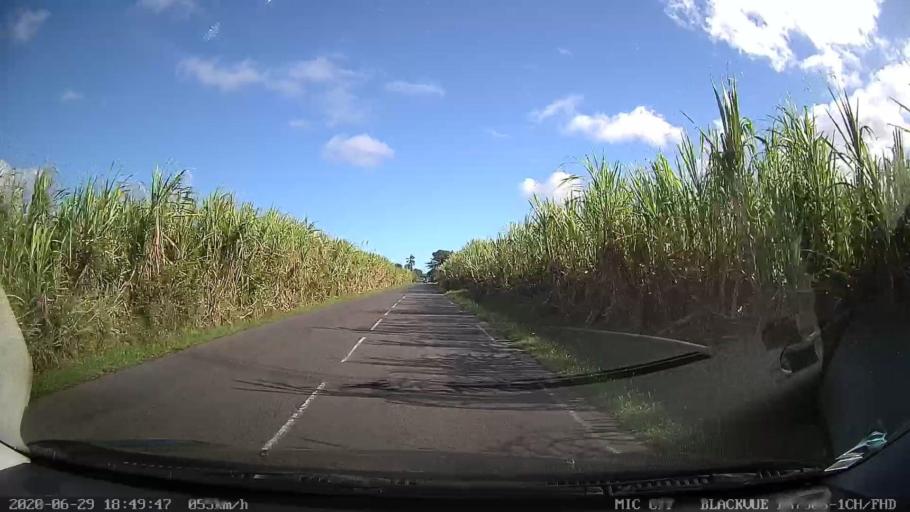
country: RE
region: Reunion
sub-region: Reunion
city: Bras-Panon
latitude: -20.9878
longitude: 55.6571
